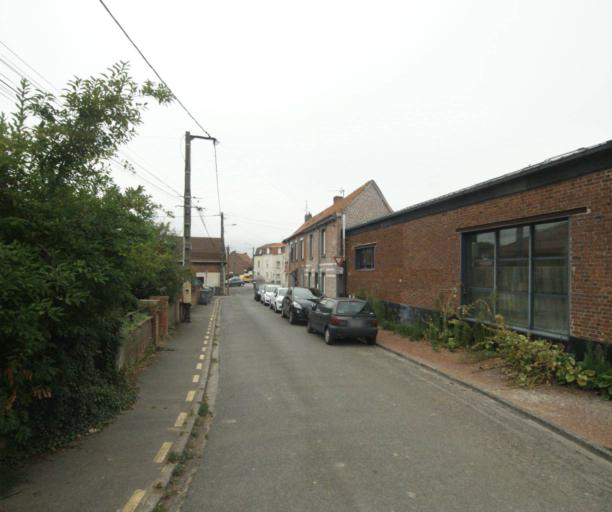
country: FR
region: Nord-Pas-de-Calais
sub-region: Departement du Nord
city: Baisieux
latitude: 50.6062
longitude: 3.2563
